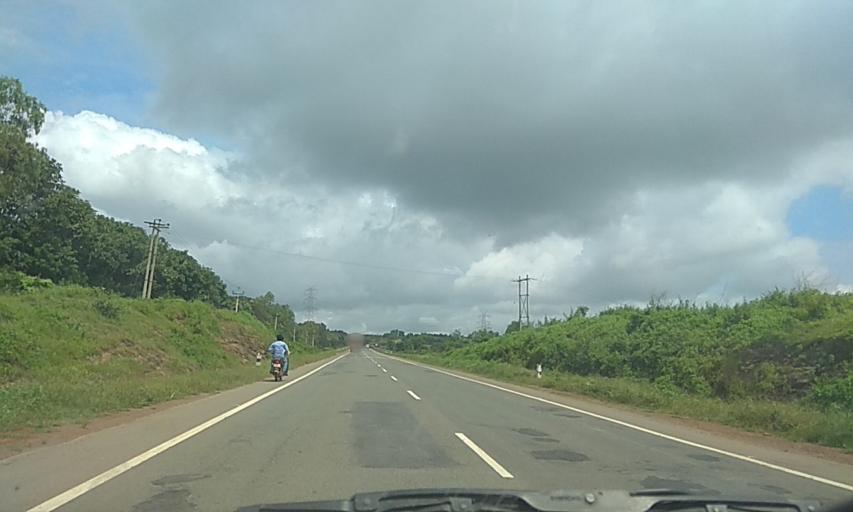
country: IN
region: Karnataka
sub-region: Dharwad
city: Hubli
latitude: 15.4278
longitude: 74.9684
